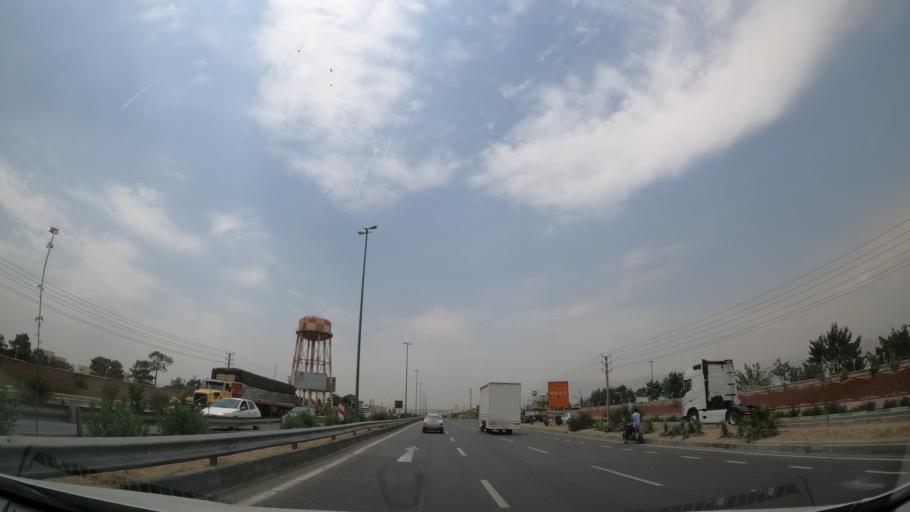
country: IR
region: Tehran
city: Shahr-e Qods
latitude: 35.6938
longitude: 51.2075
